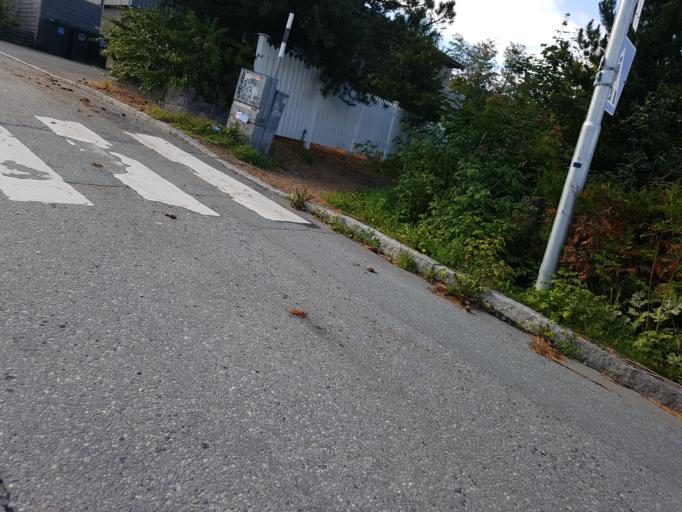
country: NO
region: Sor-Trondelag
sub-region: Trondheim
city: Trondheim
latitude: 63.4345
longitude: 10.4532
